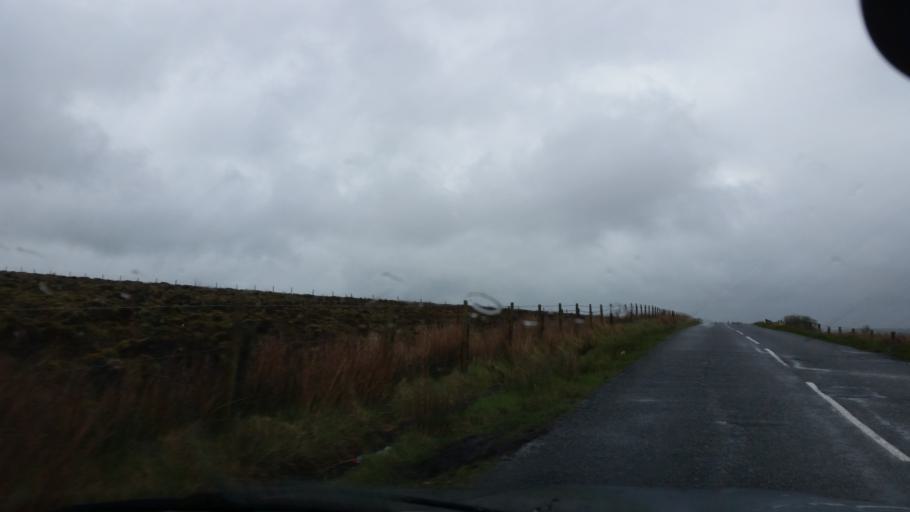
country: GB
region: Northern Ireland
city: Fintona
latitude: 54.4485
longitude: -7.3231
